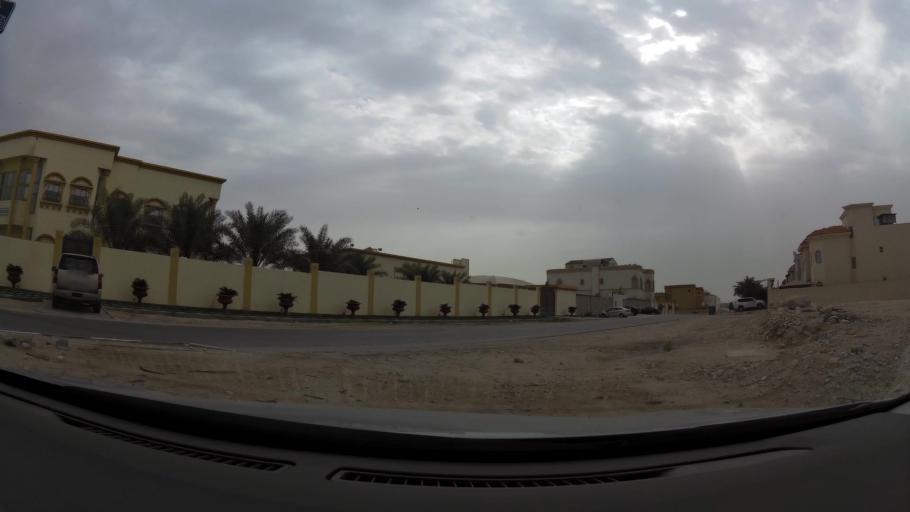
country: QA
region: Baladiyat ar Rayyan
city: Ar Rayyan
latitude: 25.3409
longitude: 51.4766
